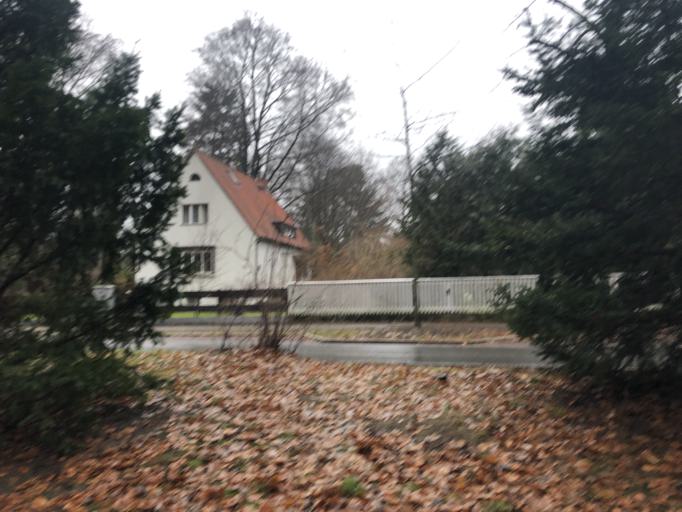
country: DE
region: Berlin
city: Frohnau
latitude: 52.6352
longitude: 13.2986
